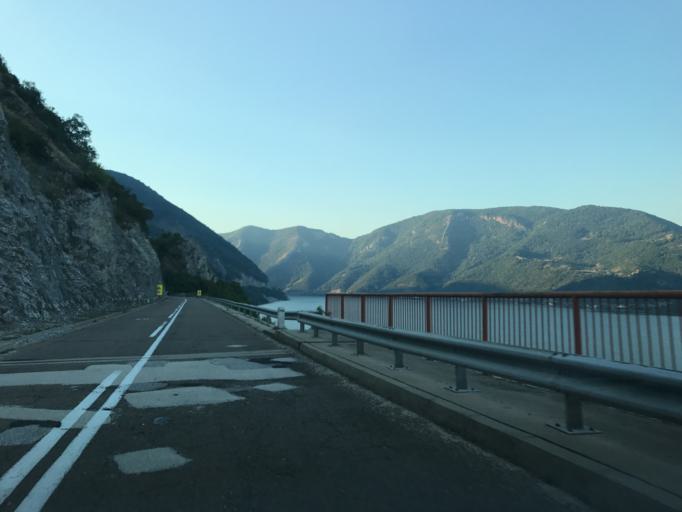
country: RO
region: Caras-Severin
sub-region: Comuna Berzasca
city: Berzasca
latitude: 44.5700
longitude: 22.0193
